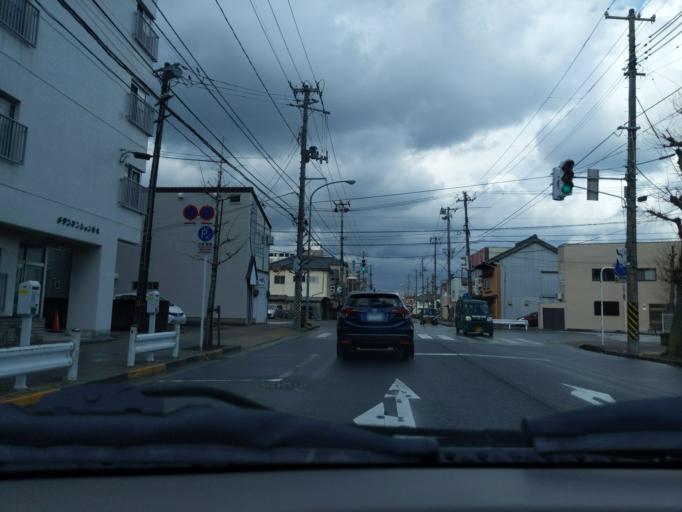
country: JP
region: Niigata
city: Niigata-shi
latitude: 37.9282
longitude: 139.0471
